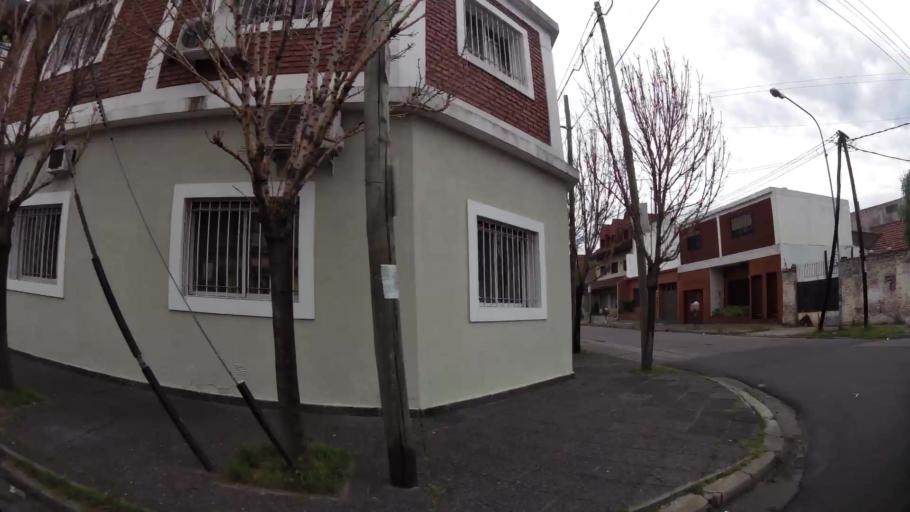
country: AR
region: Buenos Aires
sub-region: Partido de Lanus
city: Lanus
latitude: -34.6794
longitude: -58.3938
